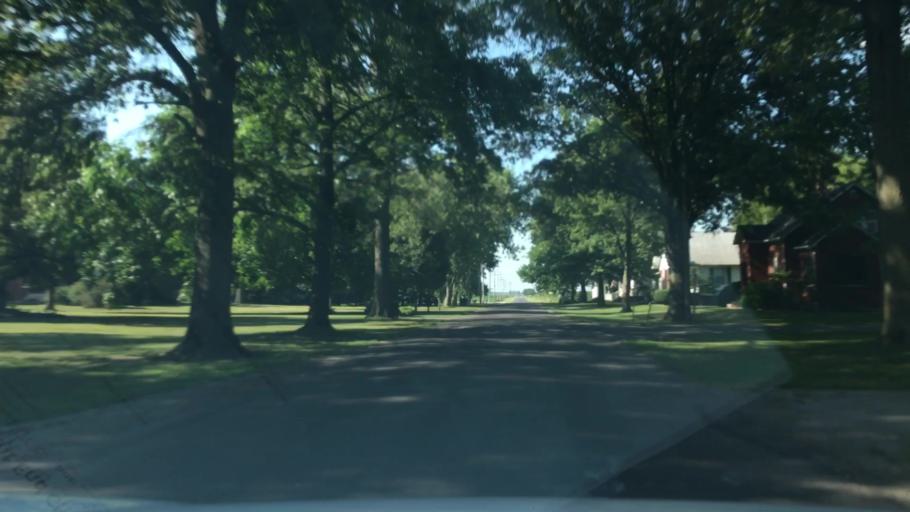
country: US
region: Illinois
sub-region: Washington County
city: Okawville
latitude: 38.3933
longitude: -89.4865
